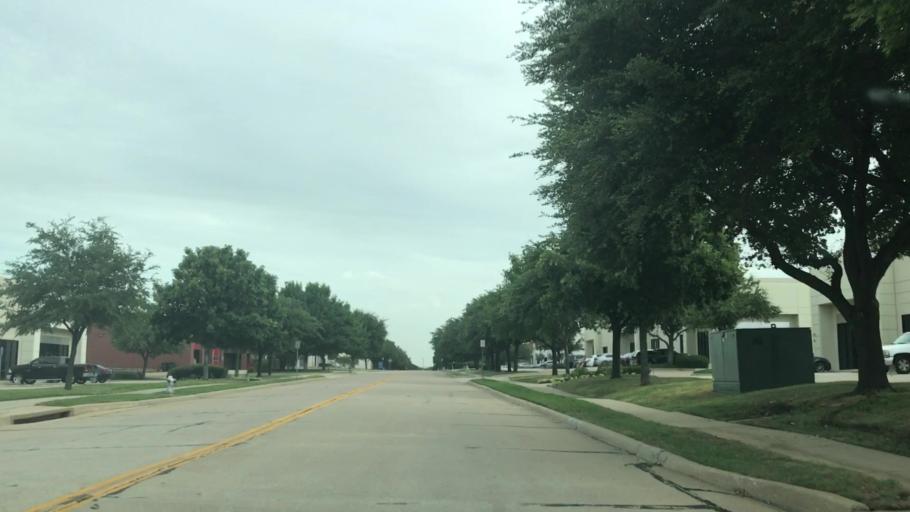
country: US
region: Texas
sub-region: Dallas County
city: Coppell
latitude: 32.9162
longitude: -97.0026
